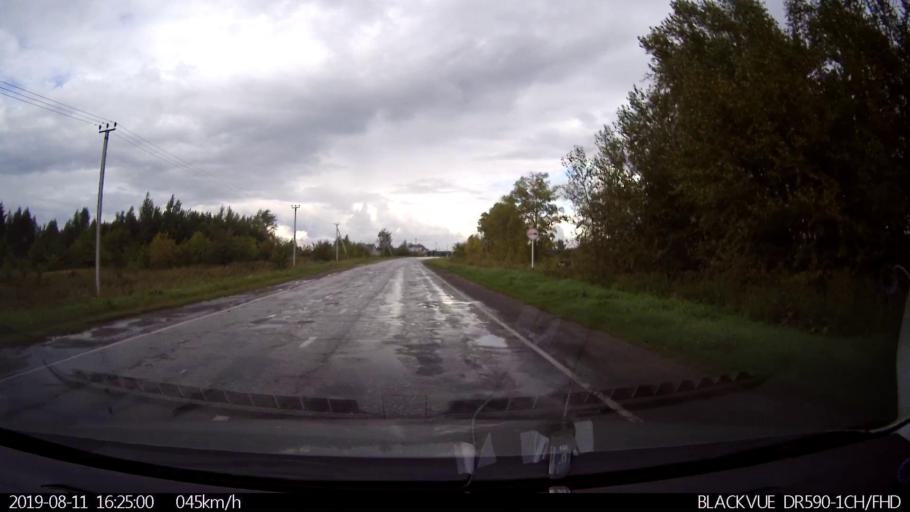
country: RU
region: Ulyanovsk
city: Mayna
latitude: 54.1038
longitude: 47.6002
